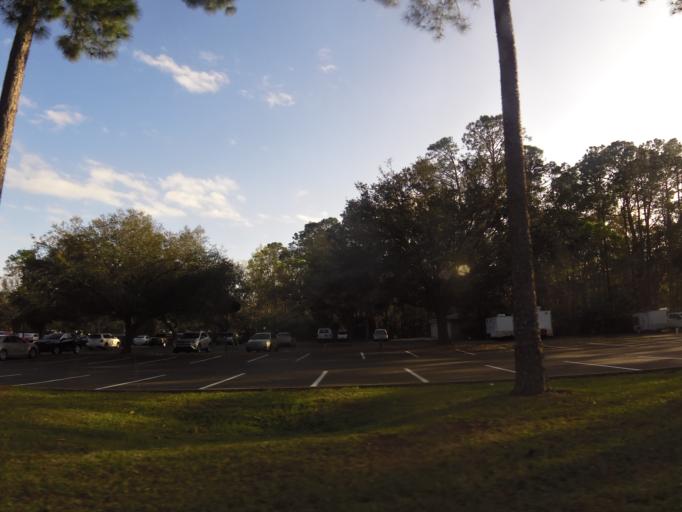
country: US
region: Florida
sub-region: Duval County
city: Jacksonville
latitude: 30.2680
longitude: -81.5756
